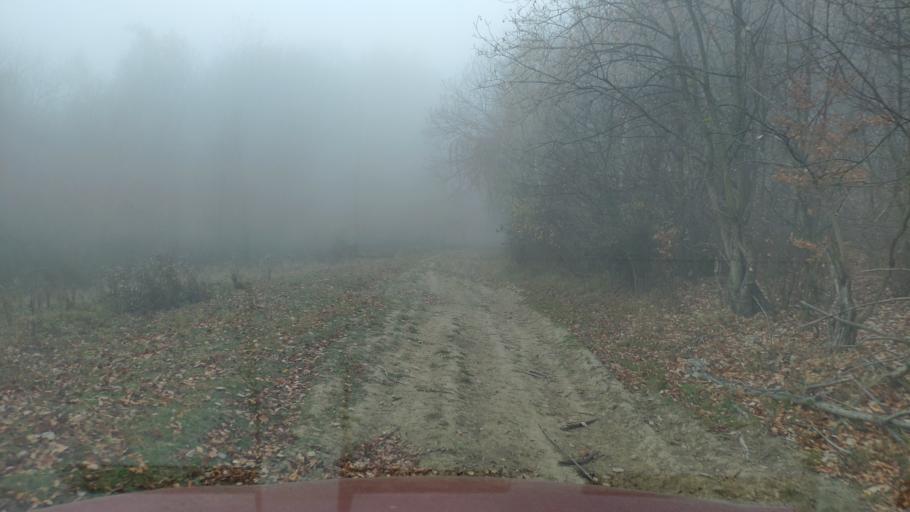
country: SK
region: Presovsky
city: Sabinov
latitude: 49.1512
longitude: 21.2289
